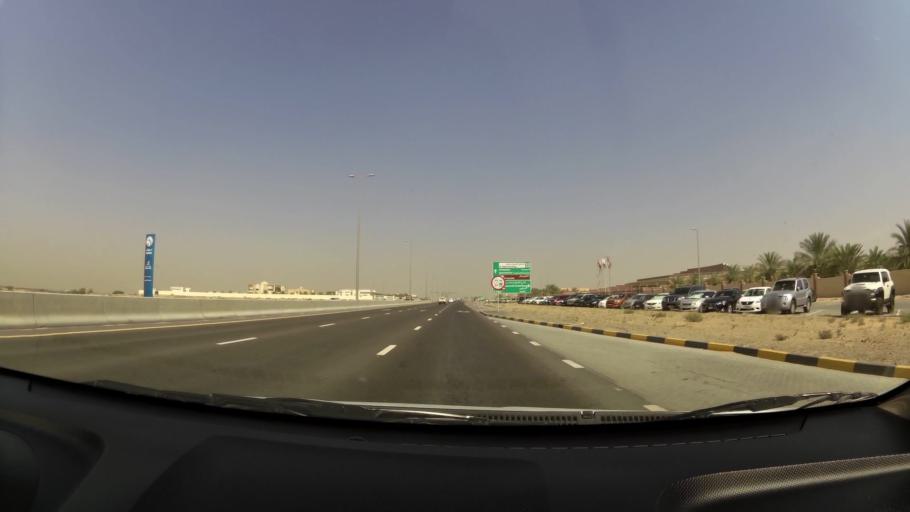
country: AE
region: Ajman
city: Ajman
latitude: 25.3886
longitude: 55.5496
